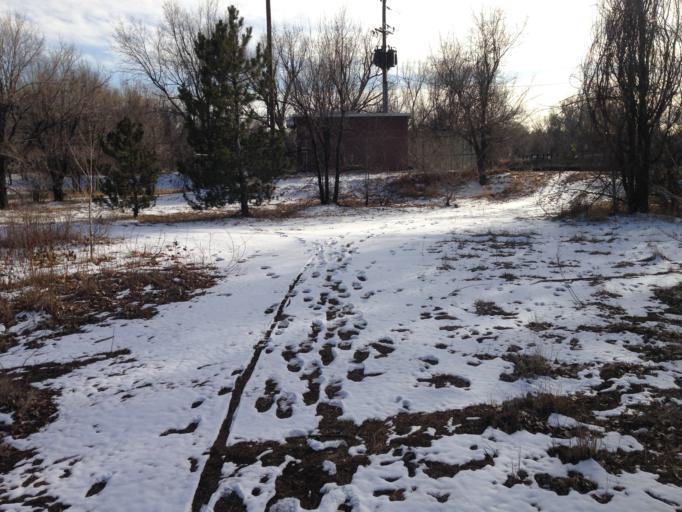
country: US
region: Colorado
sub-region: Adams County
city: Berkley
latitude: 39.7976
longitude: -105.0435
